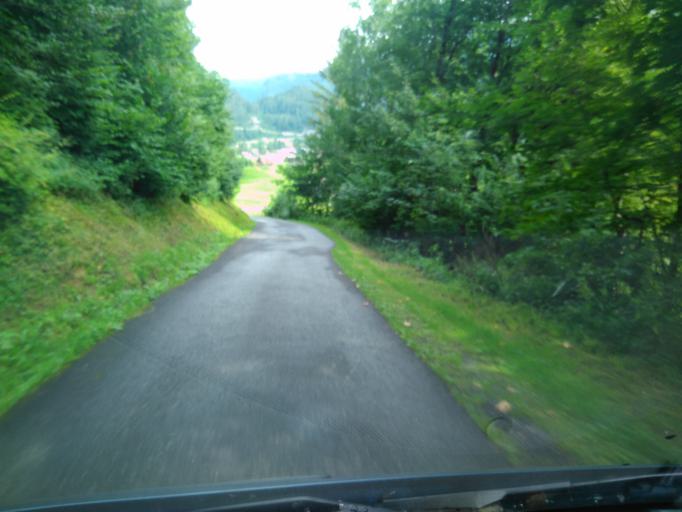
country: CH
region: Bern
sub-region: Interlaken-Oberhasli District
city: Meiringen
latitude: 46.7000
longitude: 8.2235
